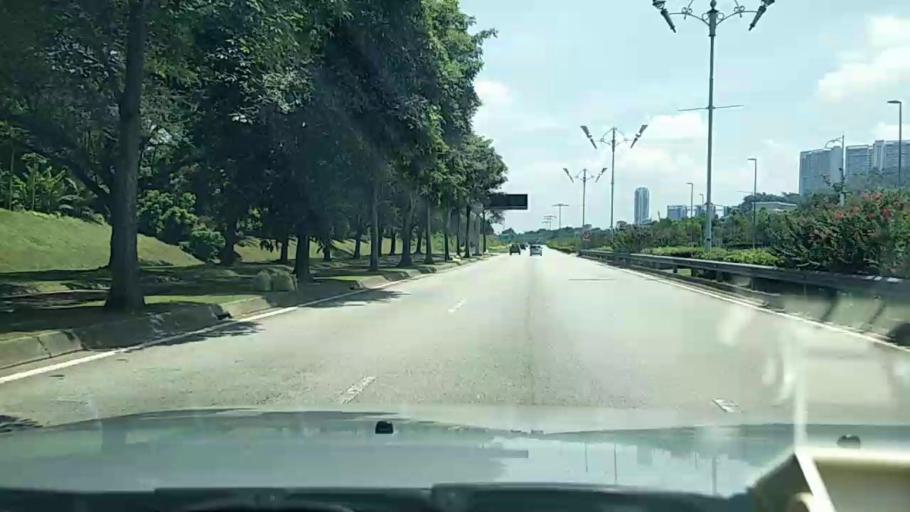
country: MY
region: Putrajaya
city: Putrajaya
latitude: 2.9462
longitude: 101.6755
